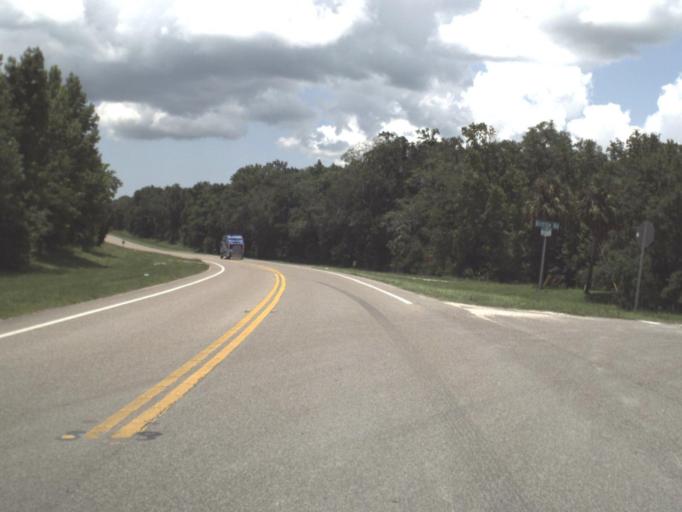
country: US
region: Florida
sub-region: Hernando County
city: North Brooksville
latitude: 28.6367
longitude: -82.4260
